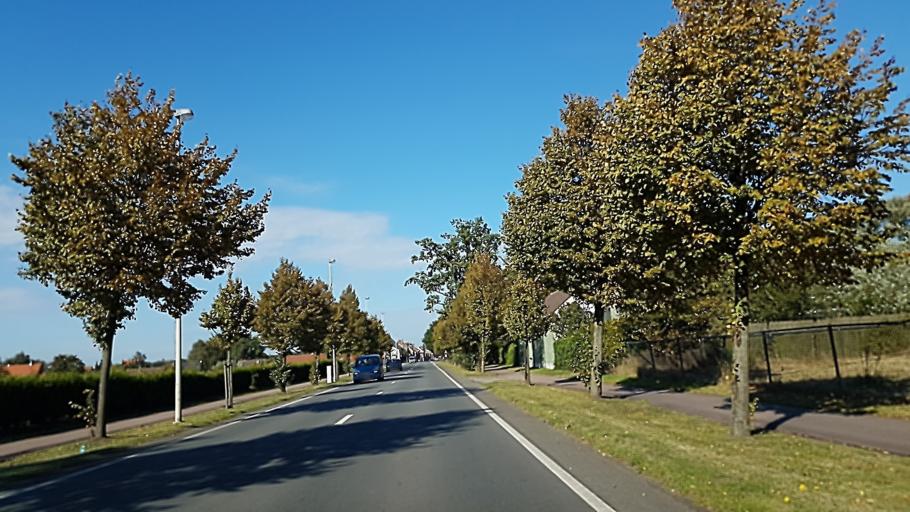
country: BE
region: Flanders
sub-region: Provincie Antwerpen
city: Kapellen
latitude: 51.3360
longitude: 4.4086
